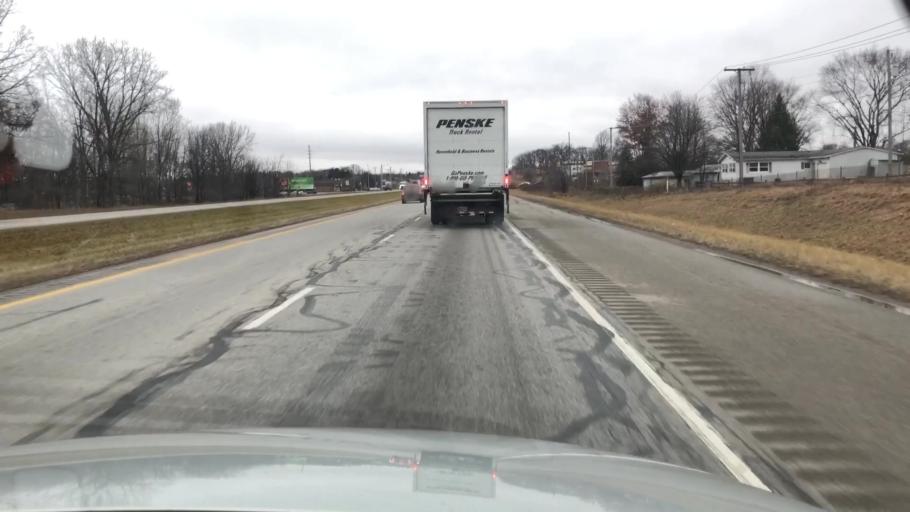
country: US
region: Indiana
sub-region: Kosciusko County
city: Winona Lake
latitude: 41.2440
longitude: -85.8205
